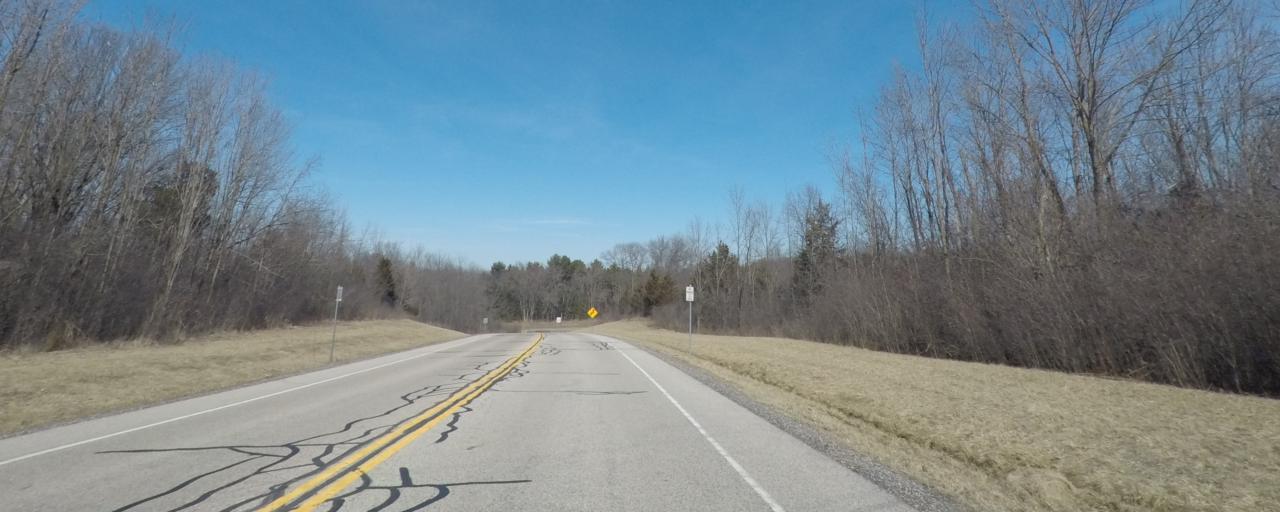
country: US
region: Wisconsin
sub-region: Waukesha County
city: Hartland
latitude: 43.1164
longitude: -88.3551
